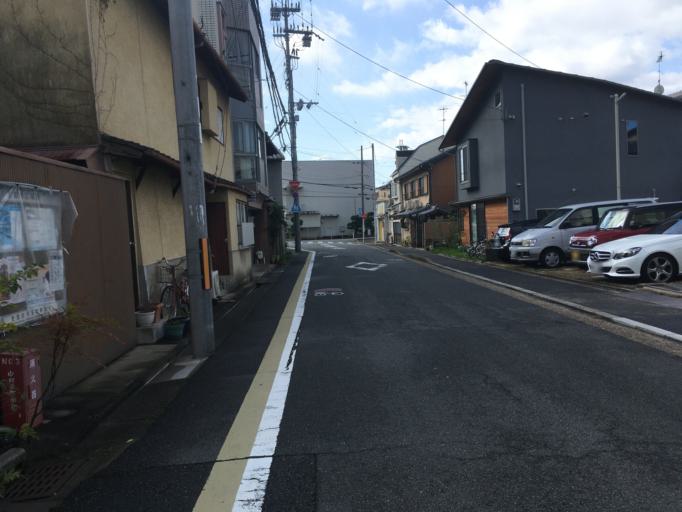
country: JP
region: Kyoto
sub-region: Kyoto-shi
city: Kamigyo-ku
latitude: 35.0243
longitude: 135.7761
